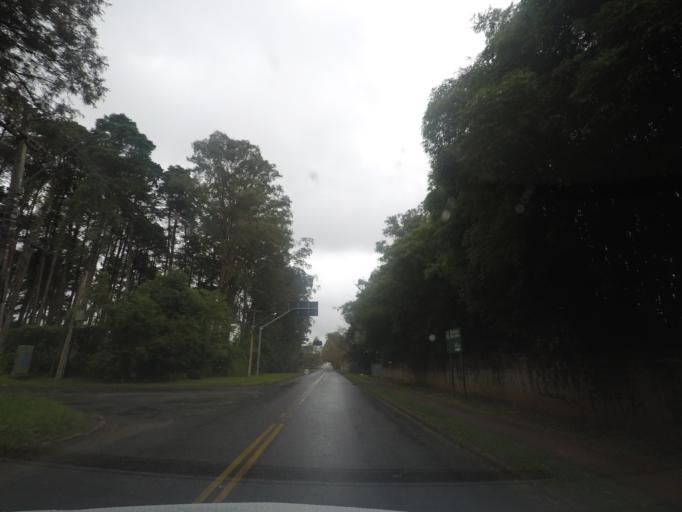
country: BR
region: Parana
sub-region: Pinhais
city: Pinhais
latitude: -25.3904
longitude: -49.1533
